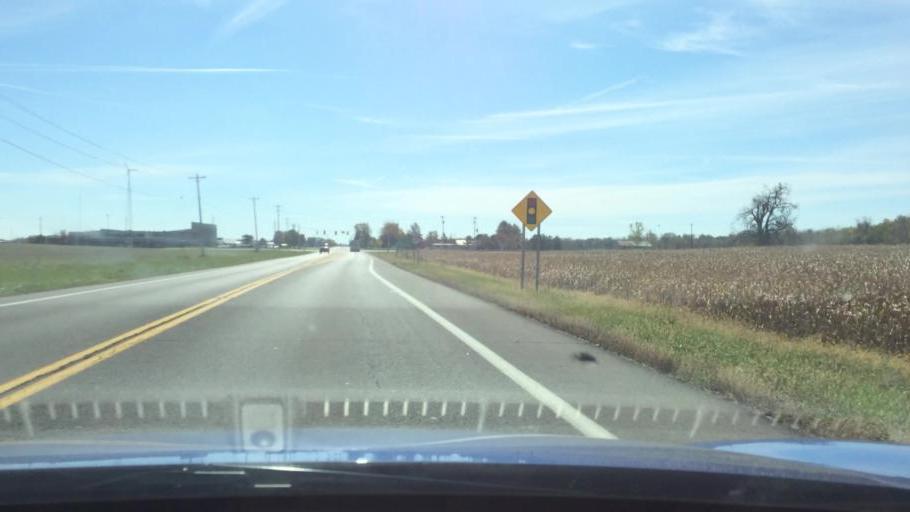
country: US
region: Ohio
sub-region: Logan County
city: Russells Point
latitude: 40.4420
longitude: -83.9060
